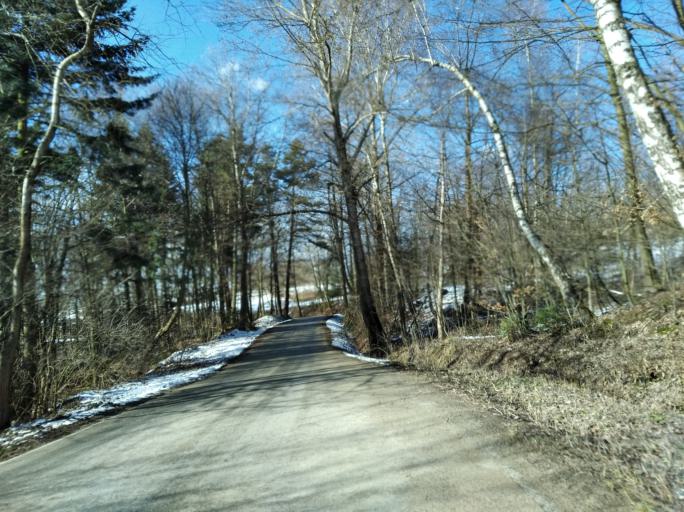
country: PL
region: Subcarpathian Voivodeship
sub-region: Powiat brzozowski
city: Jablonica Polska
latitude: 49.7201
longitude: 21.8845
